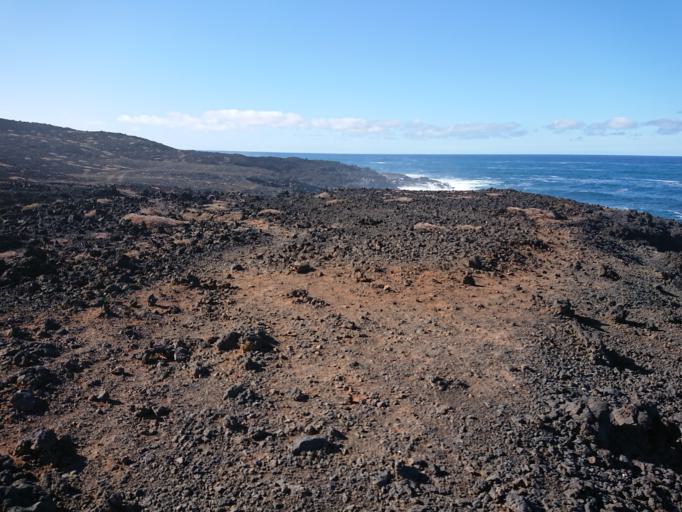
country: ES
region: Canary Islands
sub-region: Provincia de Las Palmas
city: Tinajo
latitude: 29.0811
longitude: -13.7272
